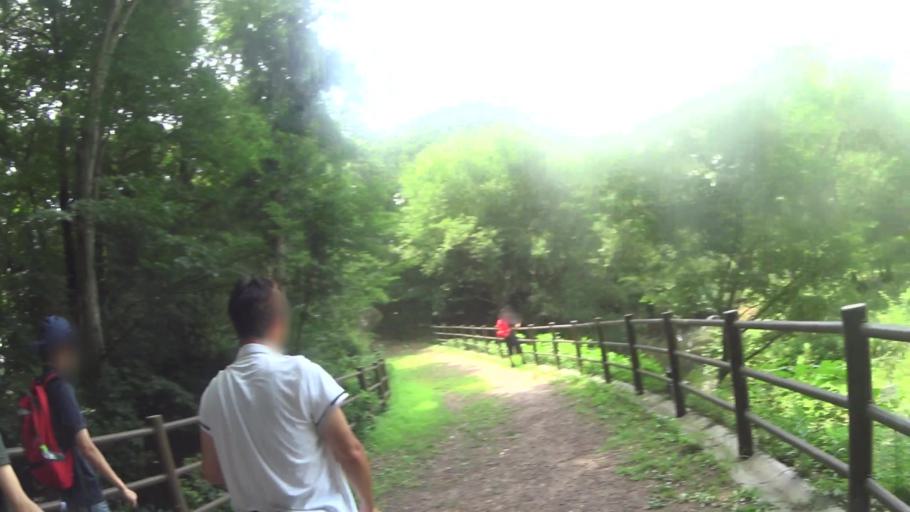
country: JP
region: Saitama
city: Ageoshimo
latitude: 35.9366
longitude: 139.5652
